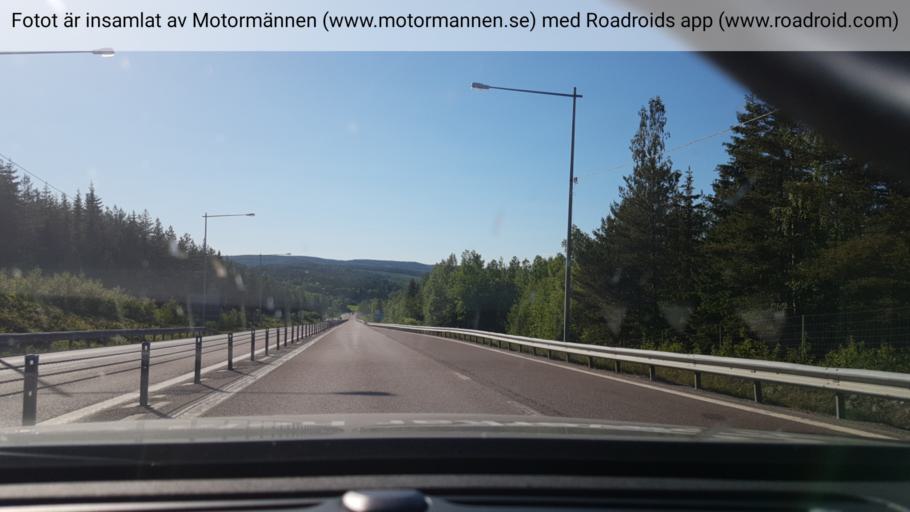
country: SE
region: Vaesternorrland
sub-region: Haernoesands Kommun
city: Haernoesand
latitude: 62.6552
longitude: 17.8785
